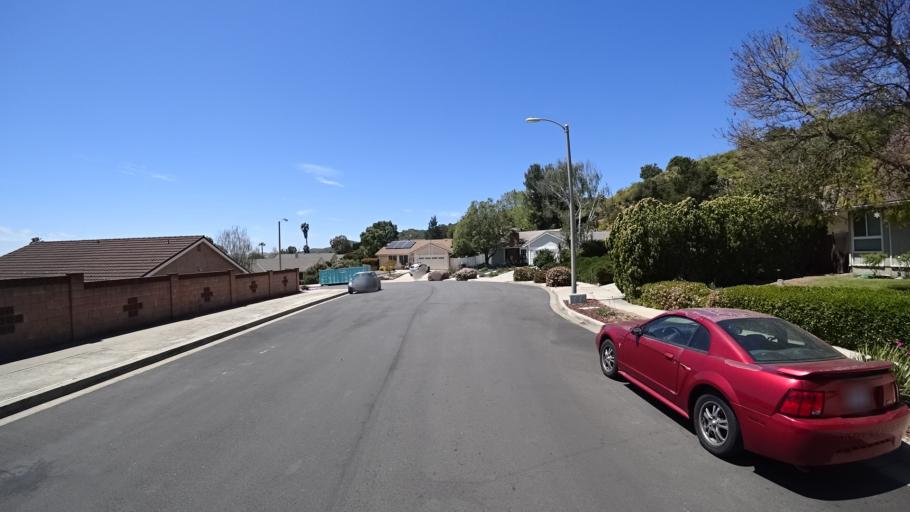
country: US
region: California
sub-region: Ventura County
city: Casa Conejo
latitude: 34.1660
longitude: -118.9477
